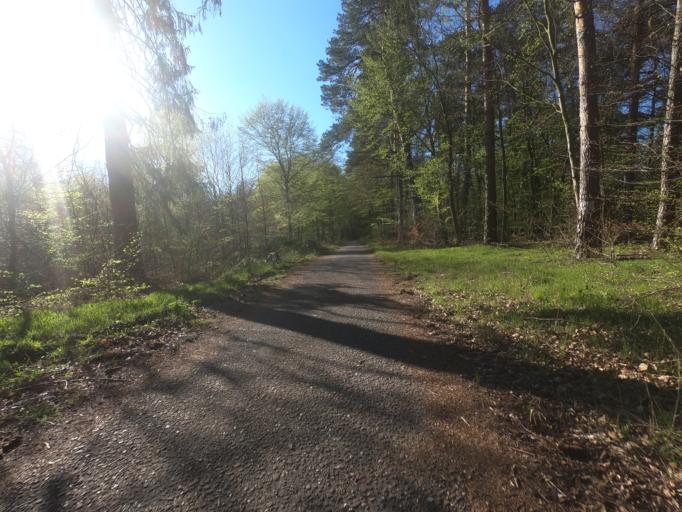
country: DE
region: Hesse
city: Langen
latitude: 49.9994
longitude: 8.6287
